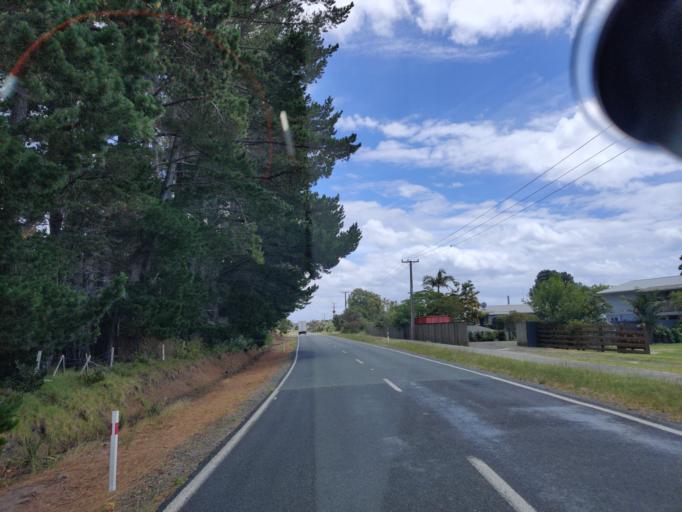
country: NZ
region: Northland
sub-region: Far North District
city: Kaitaia
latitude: -34.8233
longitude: 173.1274
